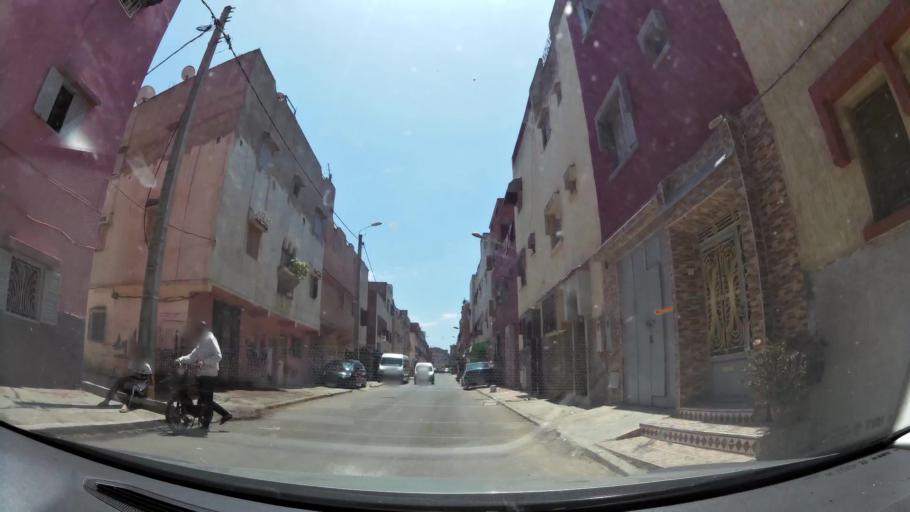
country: MA
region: Gharb-Chrarda-Beni Hssen
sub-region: Kenitra Province
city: Kenitra
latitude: 34.2582
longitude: -6.5553
